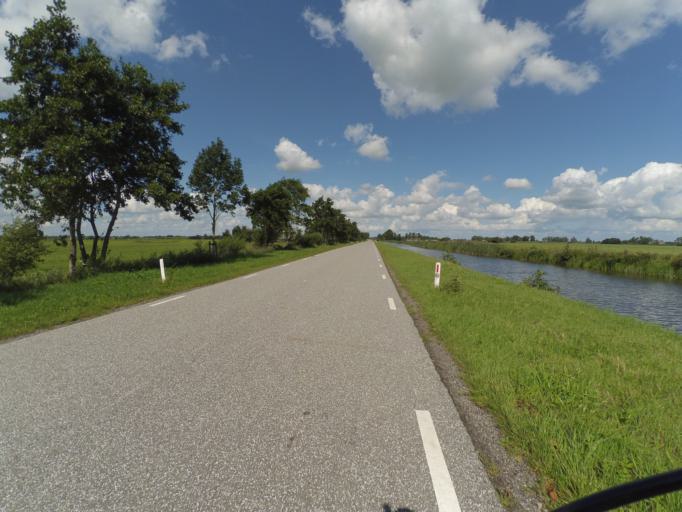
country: NL
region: Friesland
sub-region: Gemeente Achtkarspelen
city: Buitenpost
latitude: 53.2520
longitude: 6.1830
